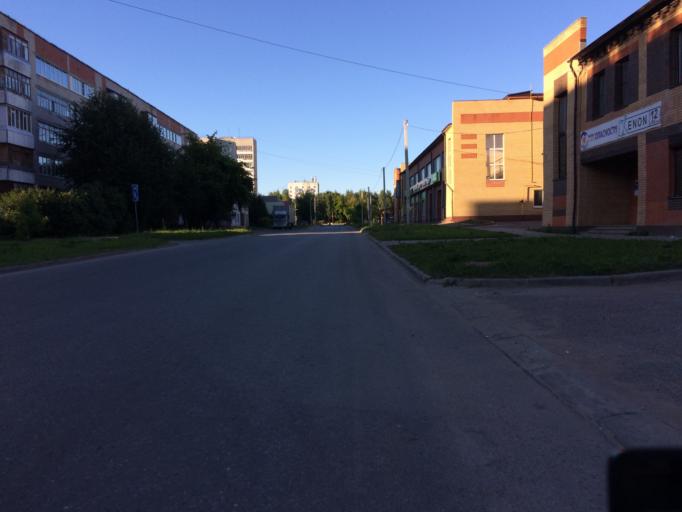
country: RU
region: Mariy-El
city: Medvedevo
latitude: 56.6437
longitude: 47.8350
